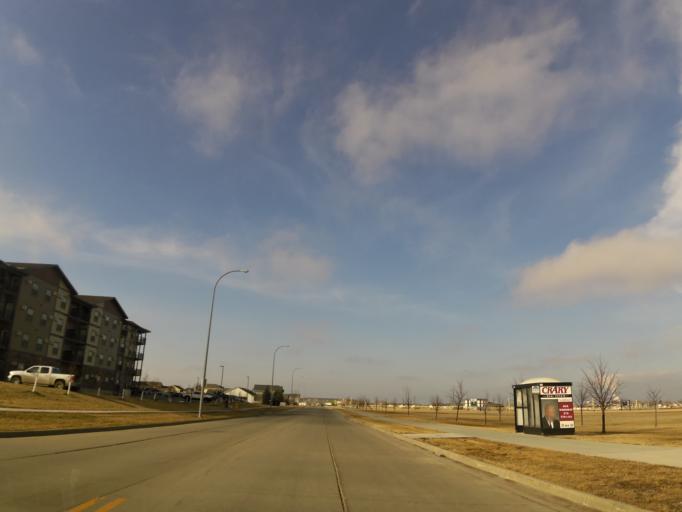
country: US
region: North Dakota
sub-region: Grand Forks County
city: Grand Forks
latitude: 47.8751
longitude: -97.0576
